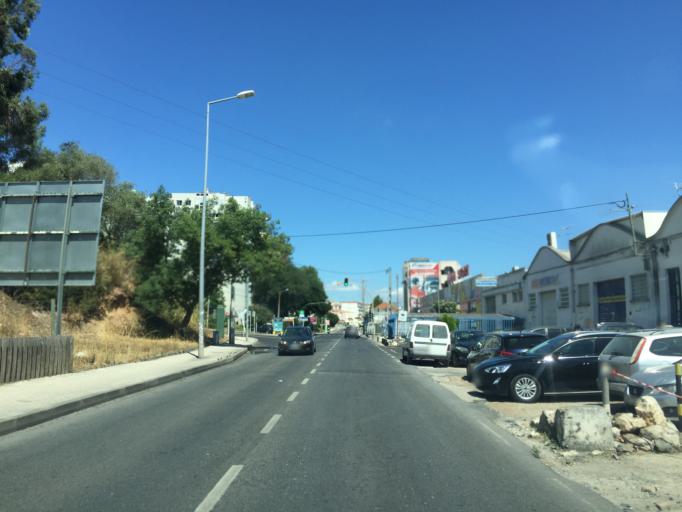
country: PT
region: Lisbon
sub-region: Odivelas
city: Povoa de Santo Adriao
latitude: 38.8056
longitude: -9.1575
